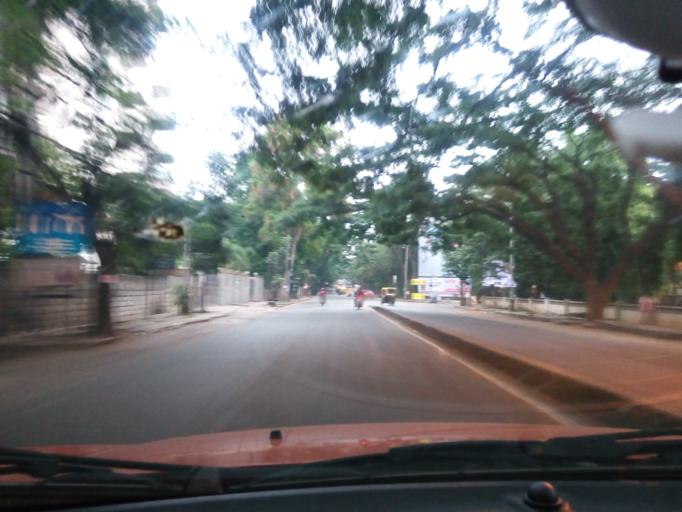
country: IN
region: Karnataka
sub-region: Bangalore Urban
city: Bangalore
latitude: 13.0148
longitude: 77.5736
